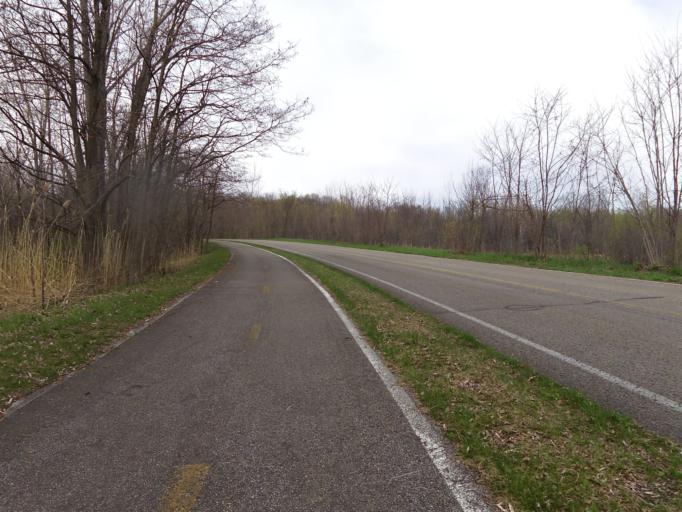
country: CA
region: Quebec
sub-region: Laurentides
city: Sainte-Marthe-sur-le-Lac
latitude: 45.4980
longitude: -74.0041
